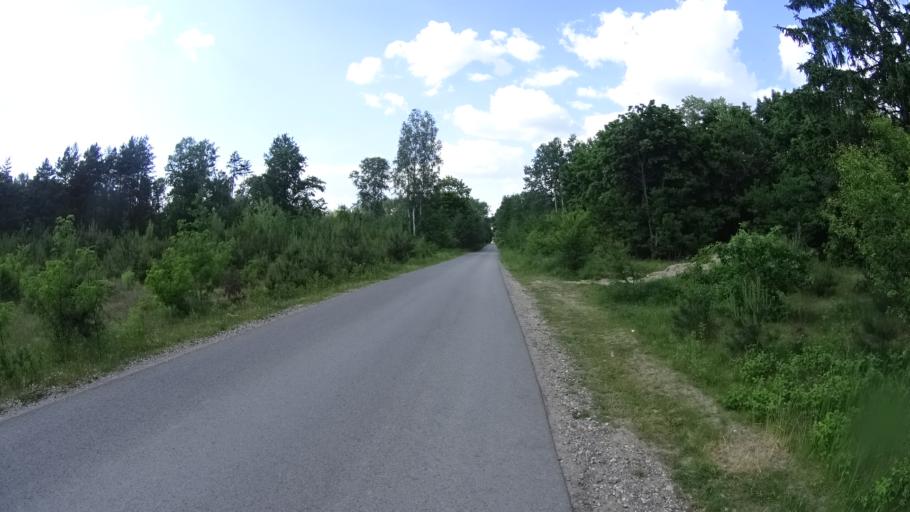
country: PL
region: Masovian Voivodeship
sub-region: Powiat pruszkowski
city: Nadarzyn
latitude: 52.0706
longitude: 20.8192
